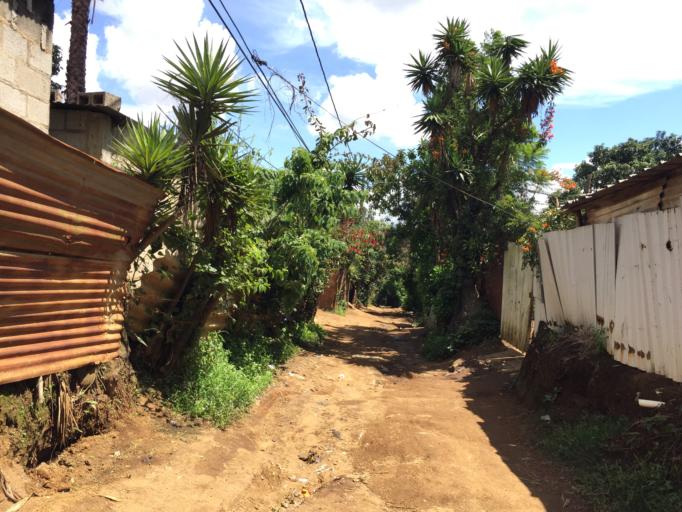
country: GT
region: Guatemala
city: Amatitlan
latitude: 14.5092
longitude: -90.6479
